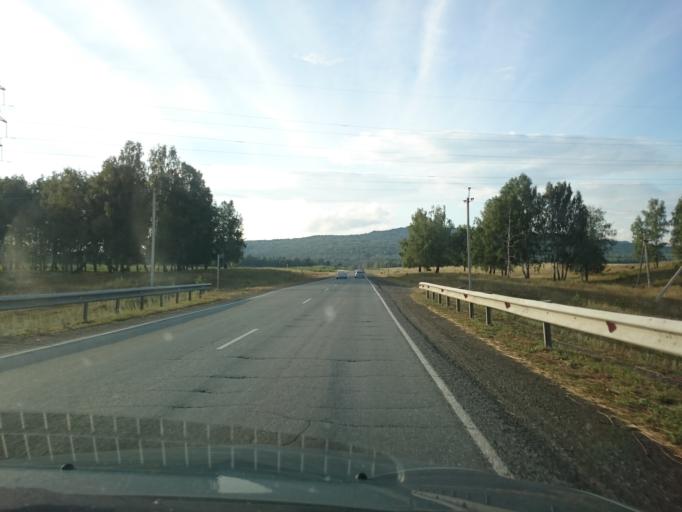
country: RU
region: Bashkortostan
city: Lomovka
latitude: 53.8870
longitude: 58.0979
